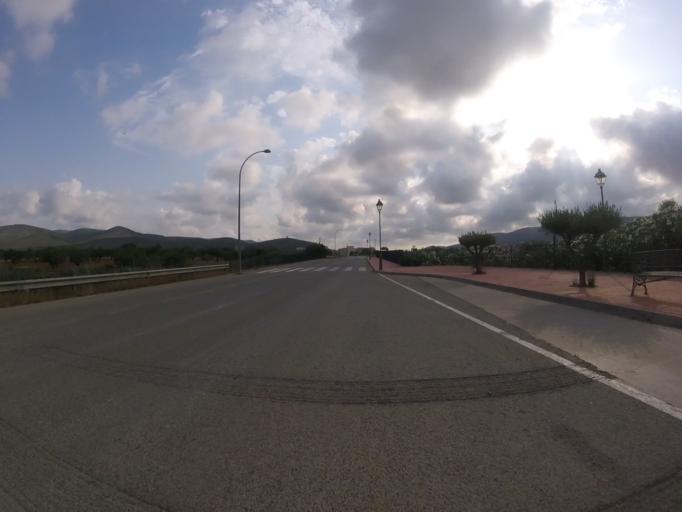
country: ES
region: Valencia
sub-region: Provincia de Castello
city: Santa Magdalena de Pulpis
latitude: 40.3557
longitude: 0.2983
